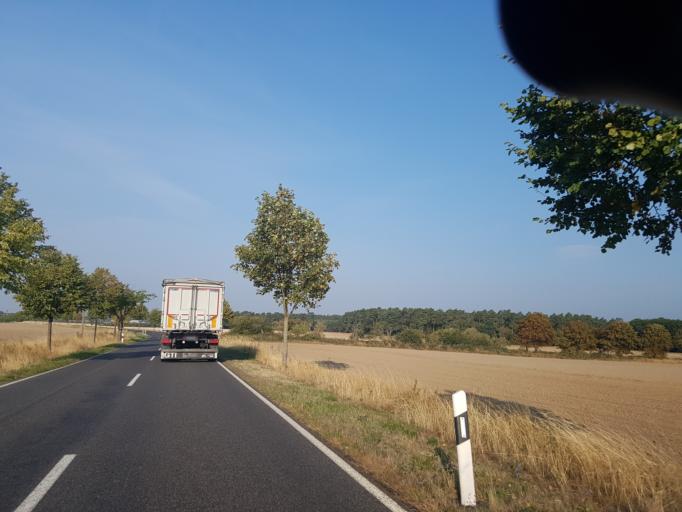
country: DE
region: Saxony-Anhalt
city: Nudersdorf
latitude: 51.9627
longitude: 12.5124
